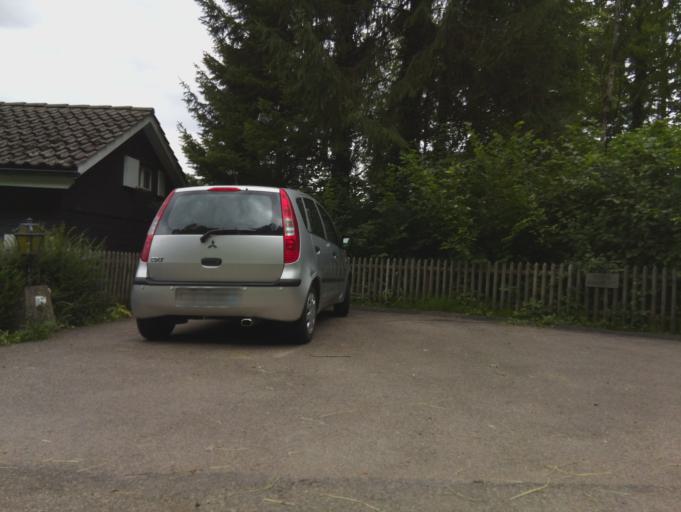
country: CH
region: Saint Gallen
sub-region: Wahlkreis Toggenburg
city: Buetschwil
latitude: 47.3581
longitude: 9.0851
